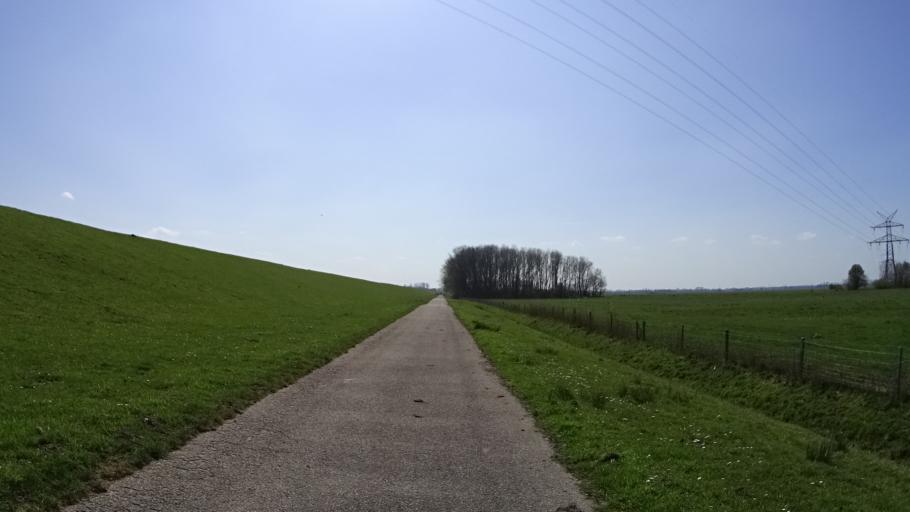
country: DE
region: Lower Saxony
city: Weener
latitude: 53.1480
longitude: 7.3703
